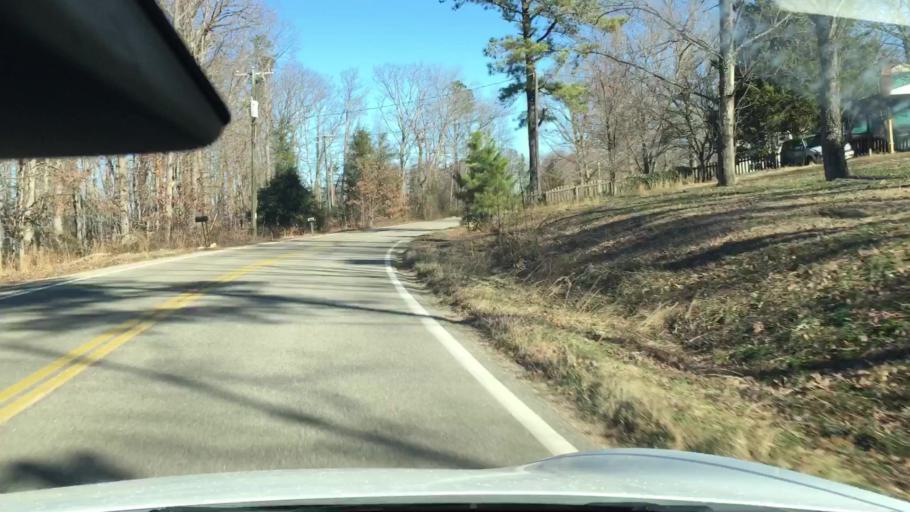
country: US
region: Virginia
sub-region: Powhatan County
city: Powhatan
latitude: 37.5408
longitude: -77.7976
